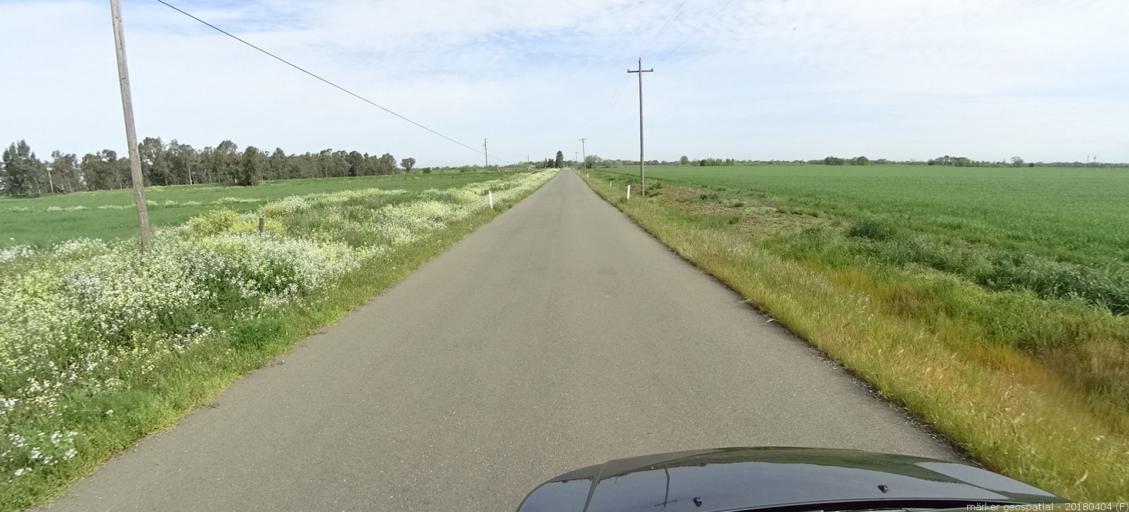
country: US
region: California
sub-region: Sacramento County
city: Herald
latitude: 38.2996
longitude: -121.2772
